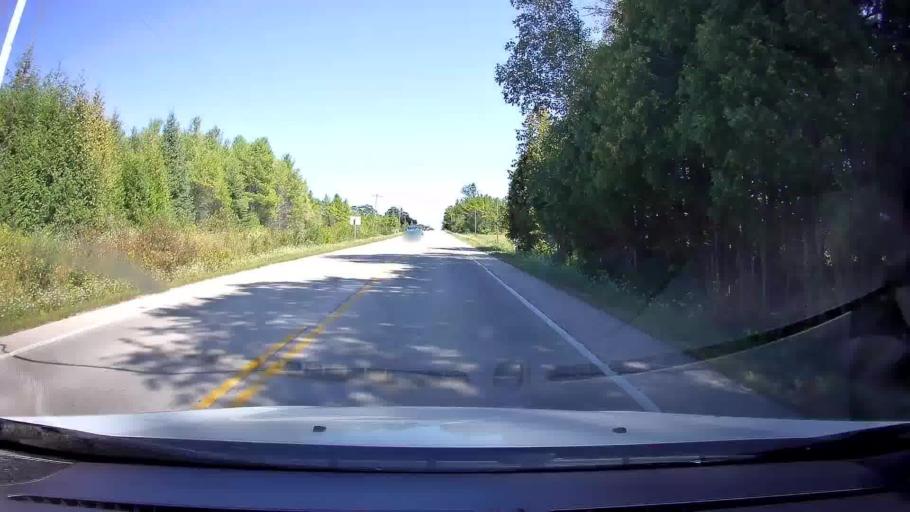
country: US
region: Michigan
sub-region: Delta County
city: Escanaba
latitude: 45.2594
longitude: -87.0492
